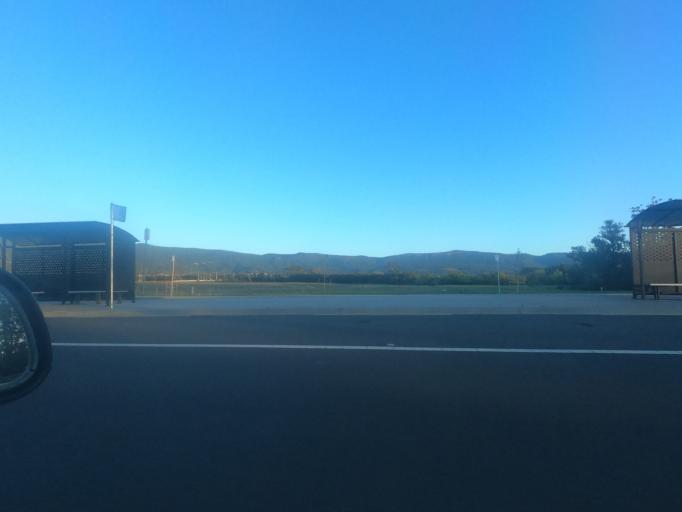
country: AU
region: New South Wales
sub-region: Wollongong
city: Dapto
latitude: -34.5015
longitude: 150.7844
